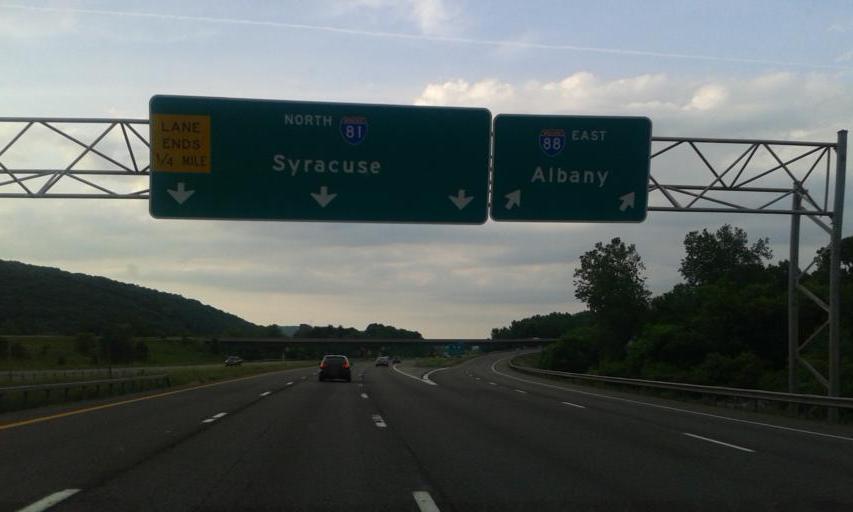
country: US
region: New York
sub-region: Broome County
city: Port Dickinson
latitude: 42.1390
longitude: -75.9020
